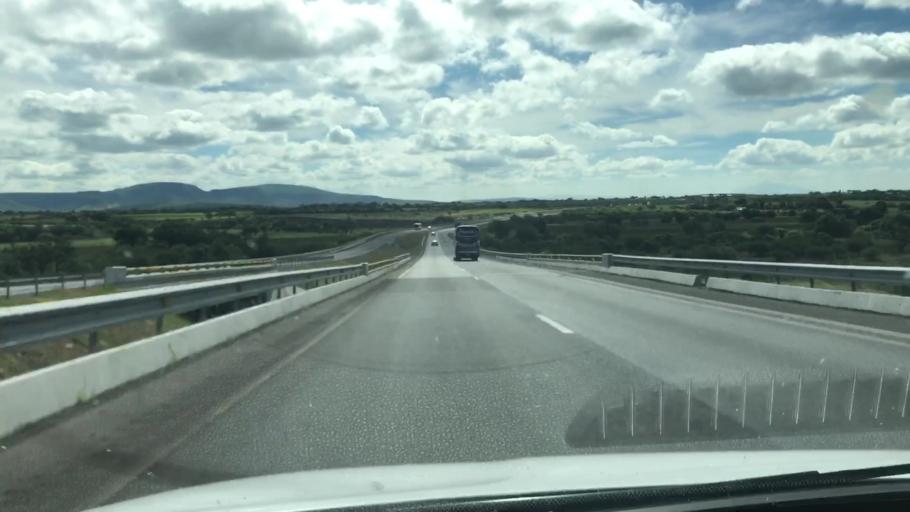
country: MX
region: Guanajuato
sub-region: Irapuato
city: Ex-Hacienda del Copal
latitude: 20.7323
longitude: -101.2952
